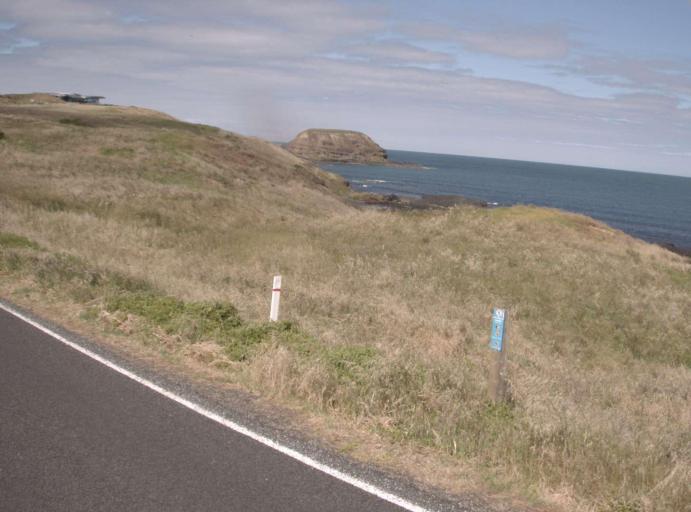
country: AU
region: Victoria
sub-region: Bass Coast
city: Phillip Island
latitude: -38.5137
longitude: 145.1223
